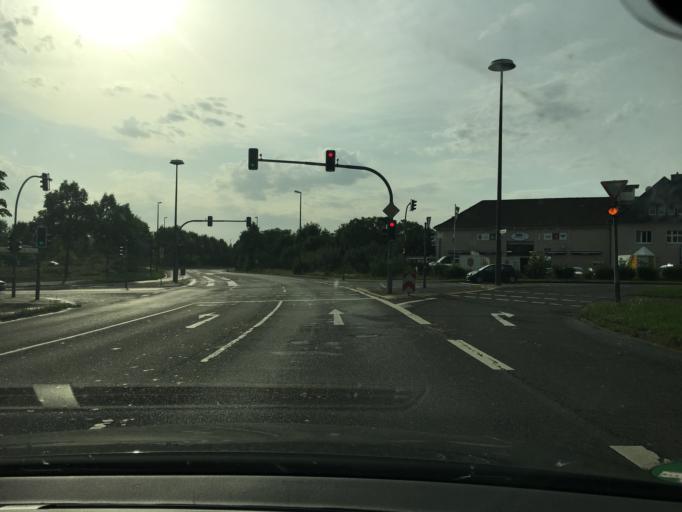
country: DE
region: North Rhine-Westphalia
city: Wesseling
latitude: 50.8200
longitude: 6.9894
